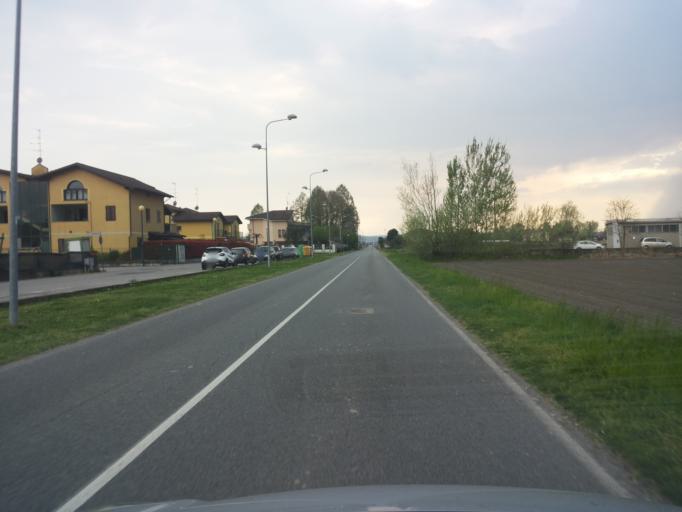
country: IT
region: Piedmont
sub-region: Provincia di Alessandria
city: Villanova Monferrato
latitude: 45.1766
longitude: 8.4779
